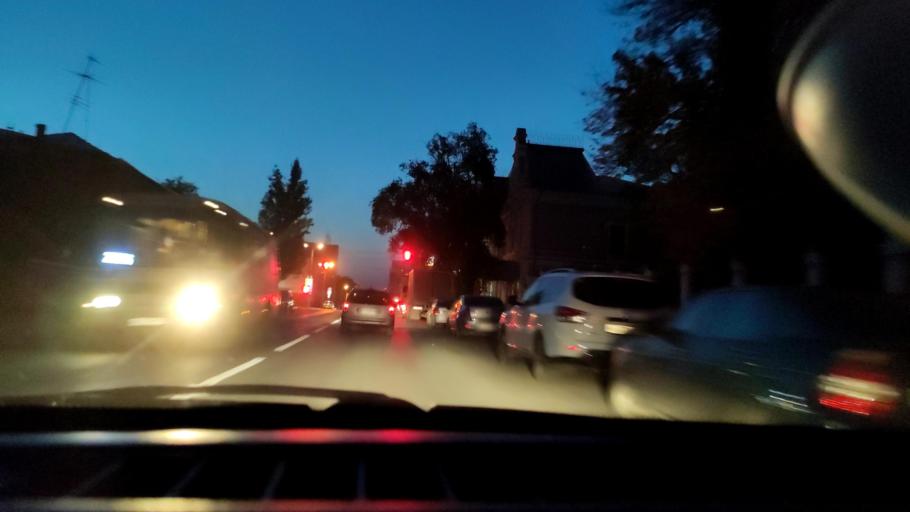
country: RU
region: Samara
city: Rozhdestveno
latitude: 53.1829
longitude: 50.0874
